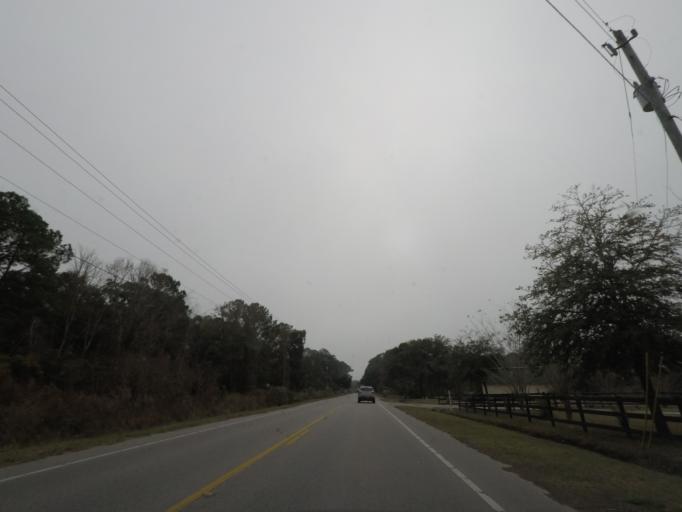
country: US
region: South Carolina
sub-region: Charleston County
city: Seabrook Island
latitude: 32.5283
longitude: -80.2964
